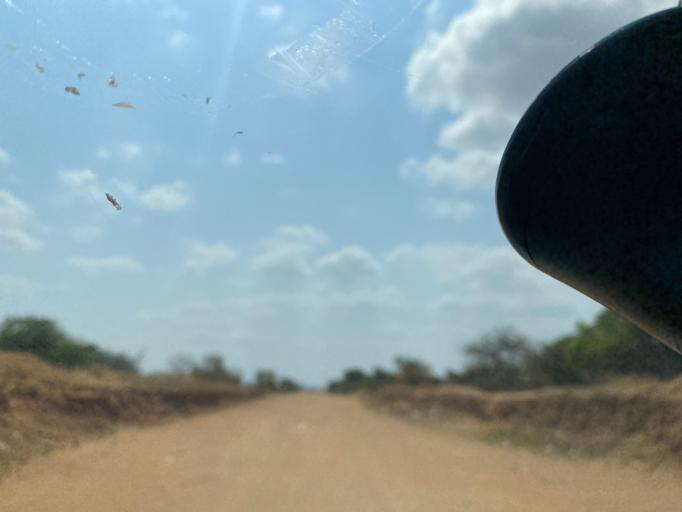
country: ZM
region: Lusaka
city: Chongwe
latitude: -15.5899
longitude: 28.7766
